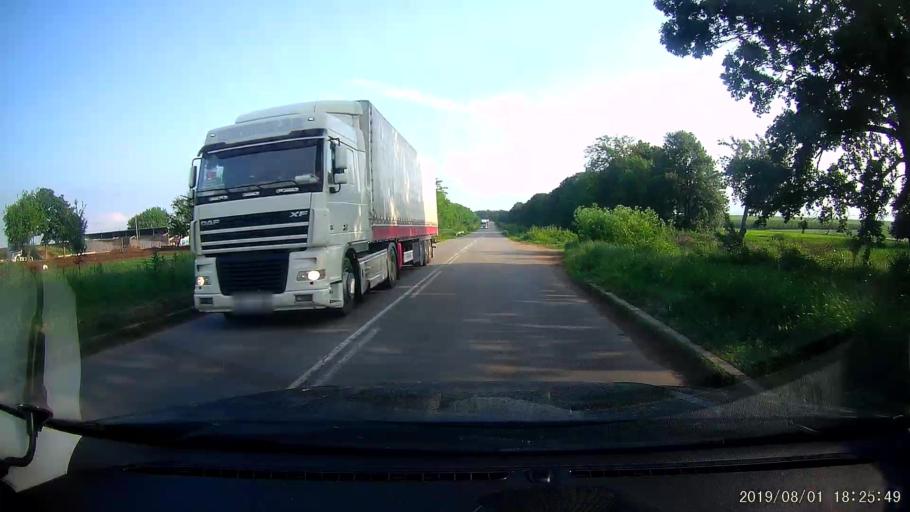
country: BG
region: Shumen
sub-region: Obshtina Venets
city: Venets
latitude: 43.6122
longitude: 26.9953
